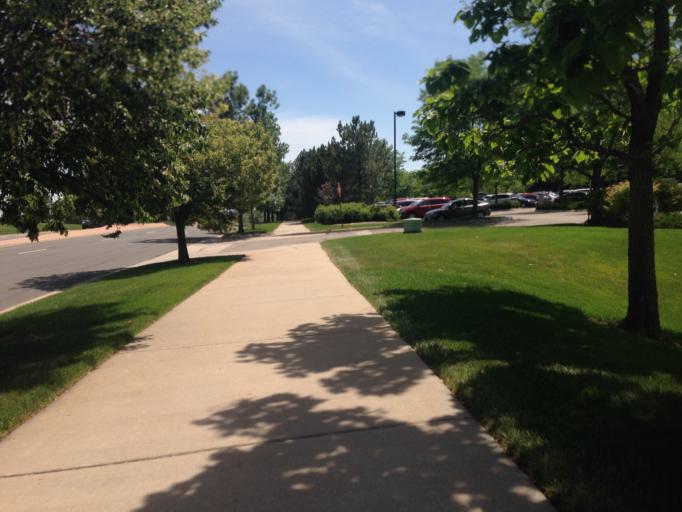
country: US
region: Colorado
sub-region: Broomfield County
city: Broomfield
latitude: 39.8990
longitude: -105.0726
